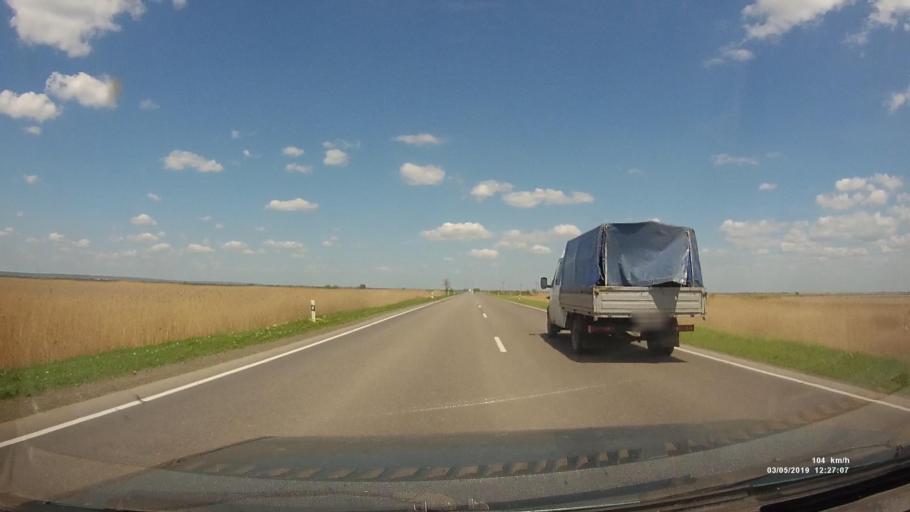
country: RU
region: Rostov
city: Semikarakorsk
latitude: 47.4551
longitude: 40.7187
